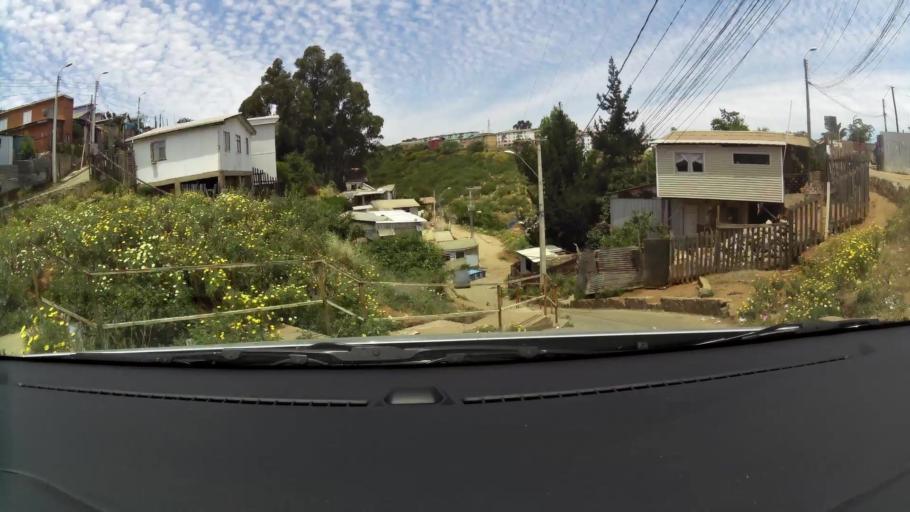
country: CL
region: Valparaiso
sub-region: Provincia de Valparaiso
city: Vina del Mar
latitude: -33.0538
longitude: -71.5652
